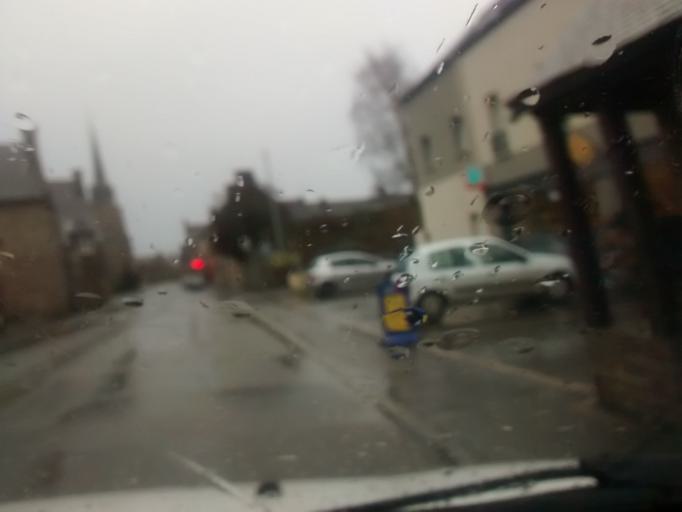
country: FR
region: Brittany
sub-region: Departement d'Ille-et-Vilaine
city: La Gouesniere
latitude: 48.5764
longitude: -1.8835
